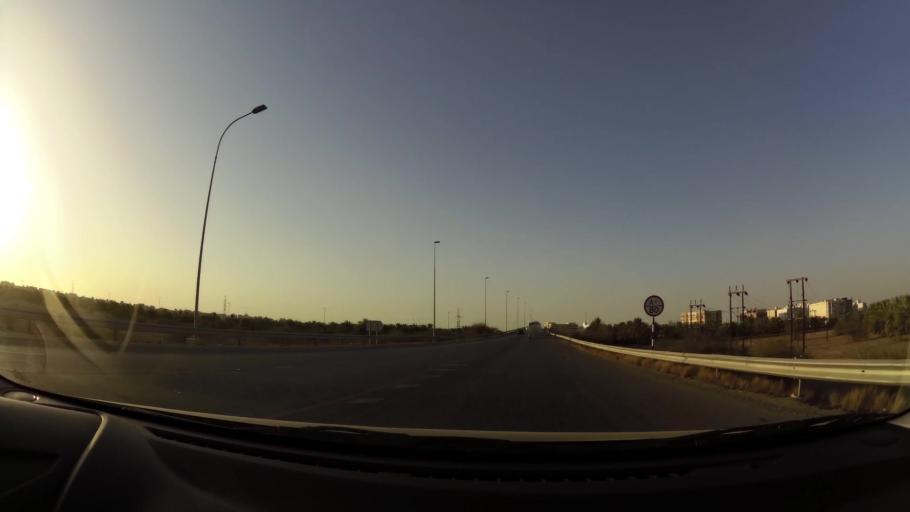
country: OM
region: Muhafazat Masqat
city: As Sib al Jadidah
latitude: 23.5891
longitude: 58.2144
